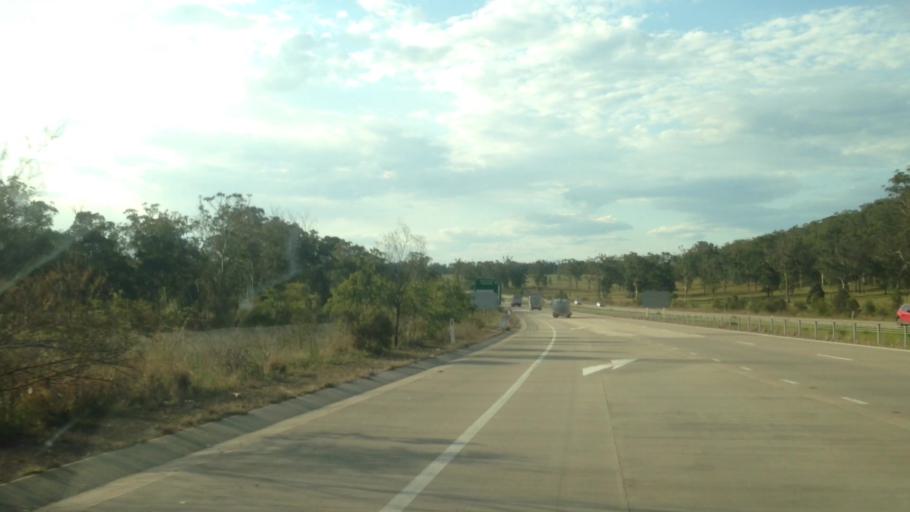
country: AU
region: New South Wales
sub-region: Cessnock
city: Heddon Greta
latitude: -32.8410
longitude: 151.5416
